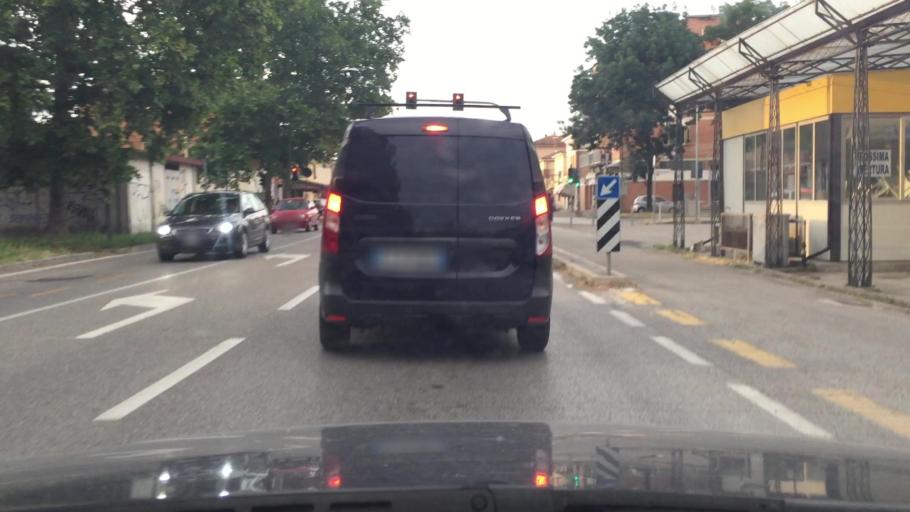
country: IT
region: Emilia-Romagna
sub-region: Provincia di Ferrara
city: Ferrara
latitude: 44.8211
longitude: 11.6052
